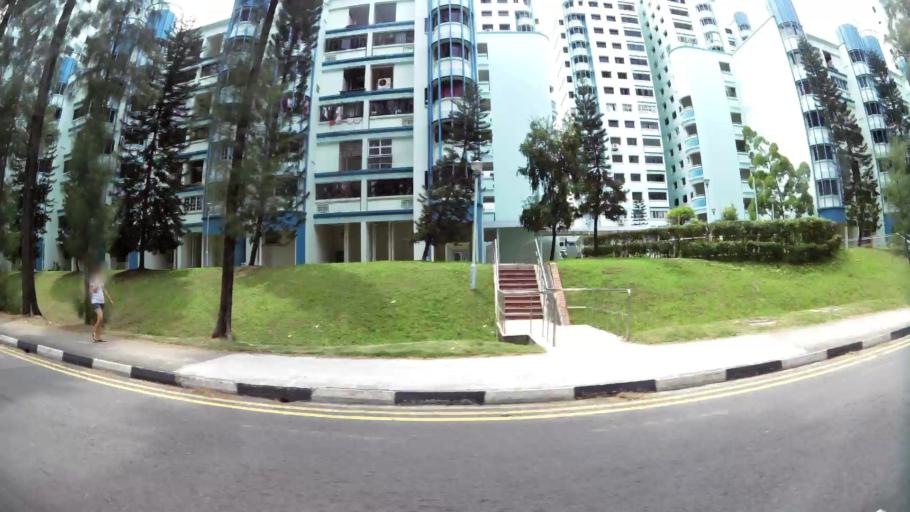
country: MY
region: Johor
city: Johor Bahru
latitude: 1.3390
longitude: 103.7239
